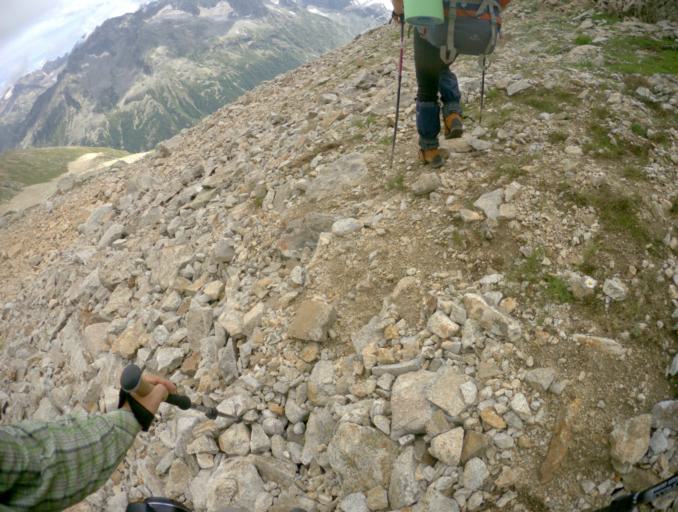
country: RU
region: Karachayevo-Cherkesiya
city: Uchkulan
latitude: 43.2761
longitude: 42.1198
